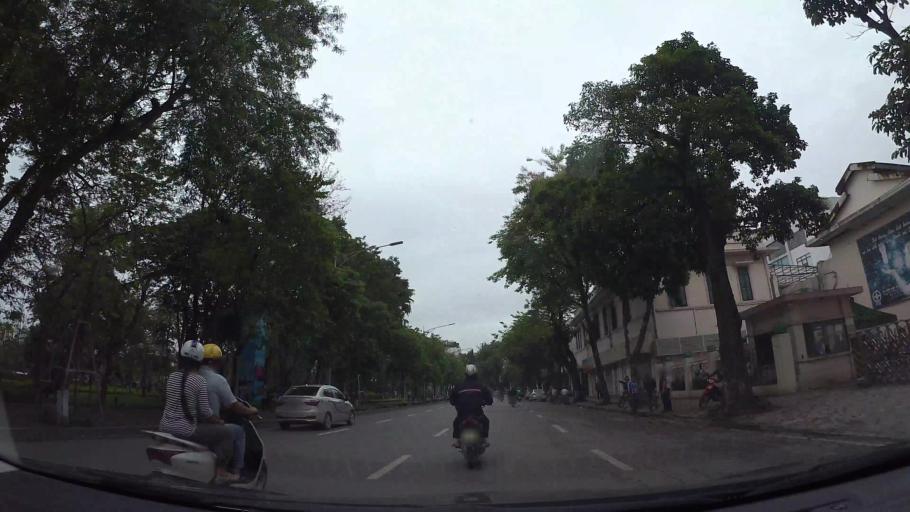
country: VN
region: Ha Noi
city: Hoan Kiem
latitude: 21.0294
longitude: 105.8539
